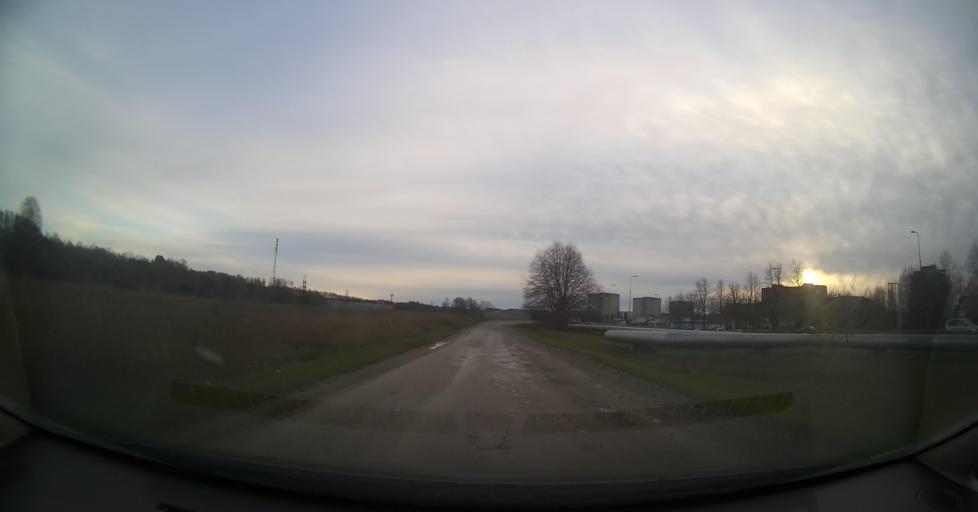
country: EE
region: Ida-Virumaa
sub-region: Johvi vald
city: Johvi
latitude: 59.3408
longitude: 27.4201
